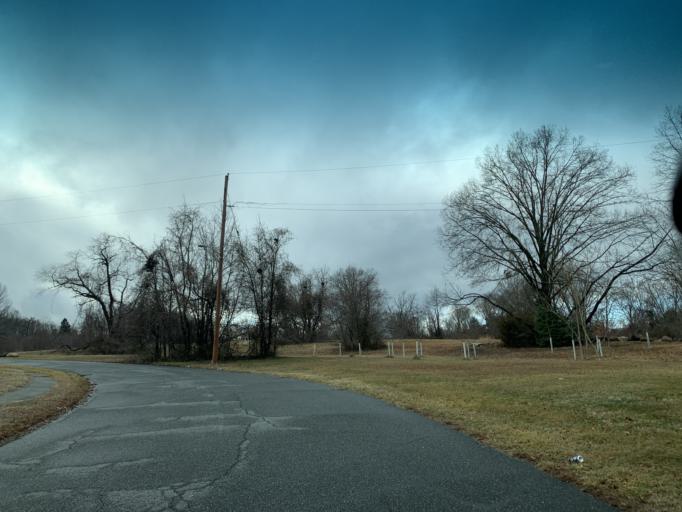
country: US
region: Maryland
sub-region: Harford County
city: Edgewood
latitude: 39.4240
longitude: -76.3032
